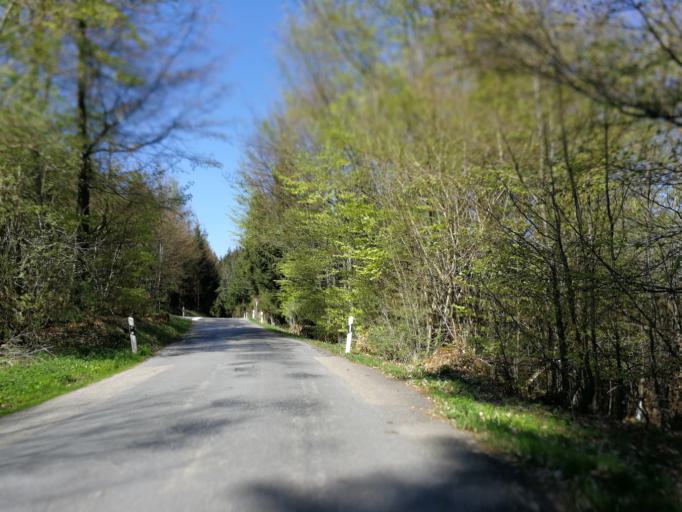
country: CH
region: Zurich
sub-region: Bezirk Uster
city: Aesch
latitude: 47.3135
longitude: 8.6594
